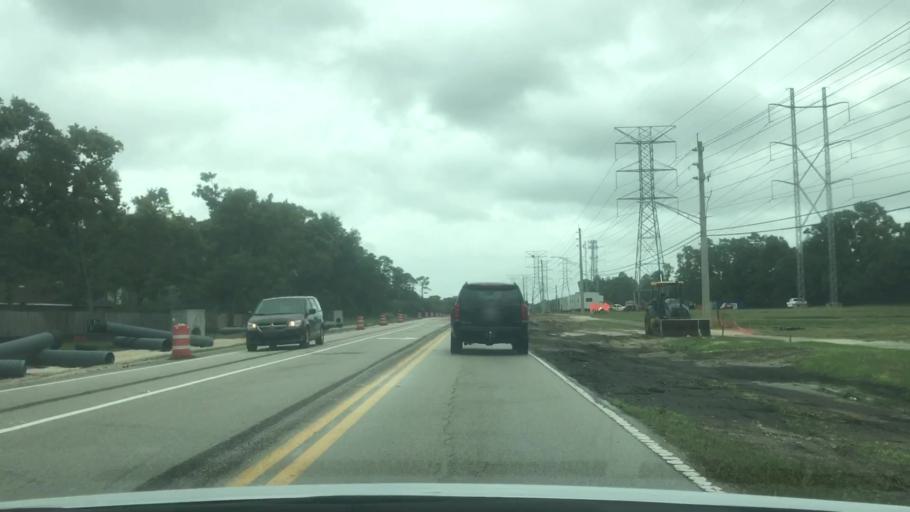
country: US
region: Florida
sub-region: Duval County
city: Atlantic Beach
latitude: 30.3545
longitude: -81.4900
